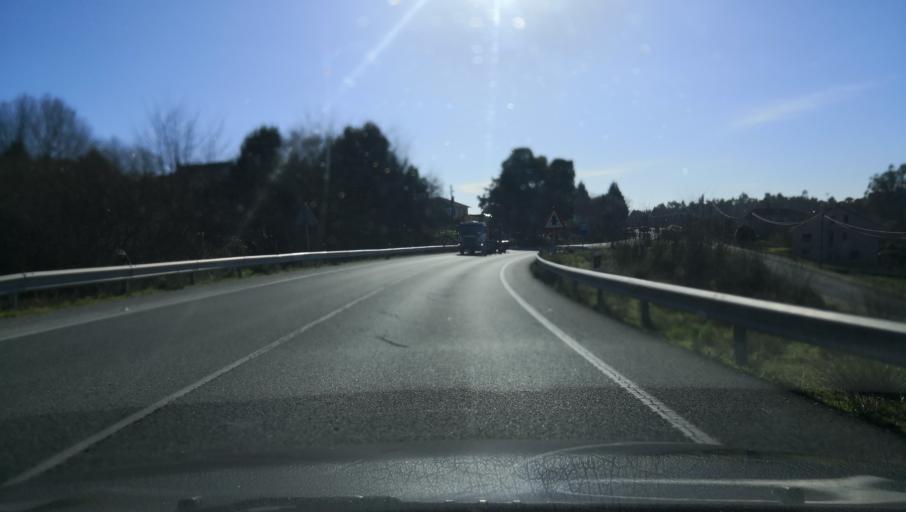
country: ES
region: Galicia
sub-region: Provincia da Coruna
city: Vedra
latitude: 42.7879
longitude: -8.4413
